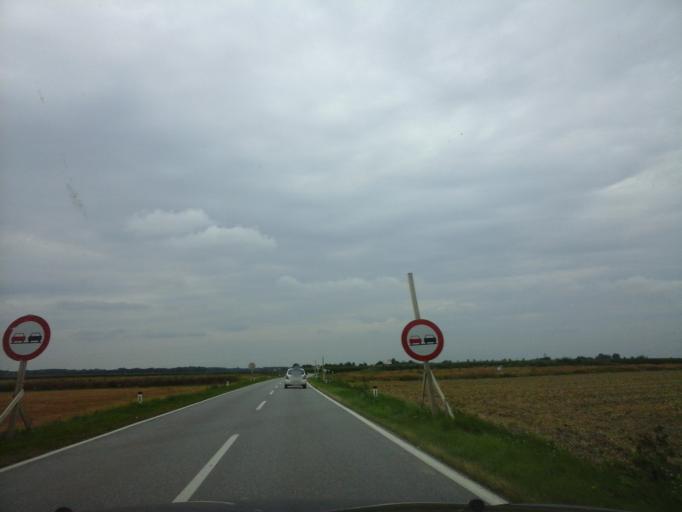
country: AT
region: Lower Austria
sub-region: Politischer Bezirk Ganserndorf
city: Orth an der Donau
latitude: 48.1570
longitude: 16.7395
